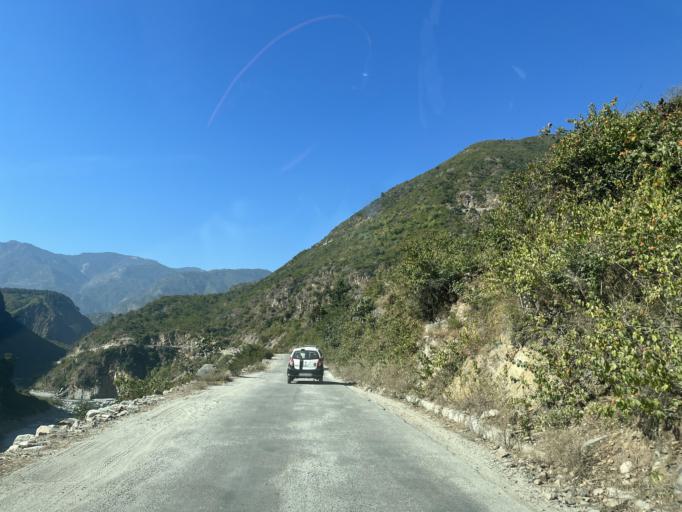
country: IN
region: Uttarakhand
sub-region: Naini Tal
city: Naini Tal
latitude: 29.5110
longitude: 79.4707
